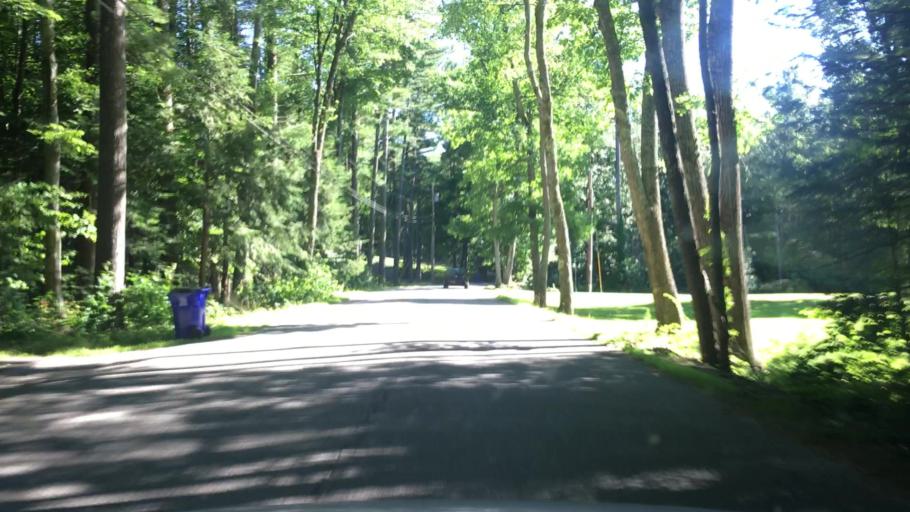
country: US
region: New Hampshire
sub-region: Rockingham County
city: Exeter
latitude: 43.0187
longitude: -70.9767
